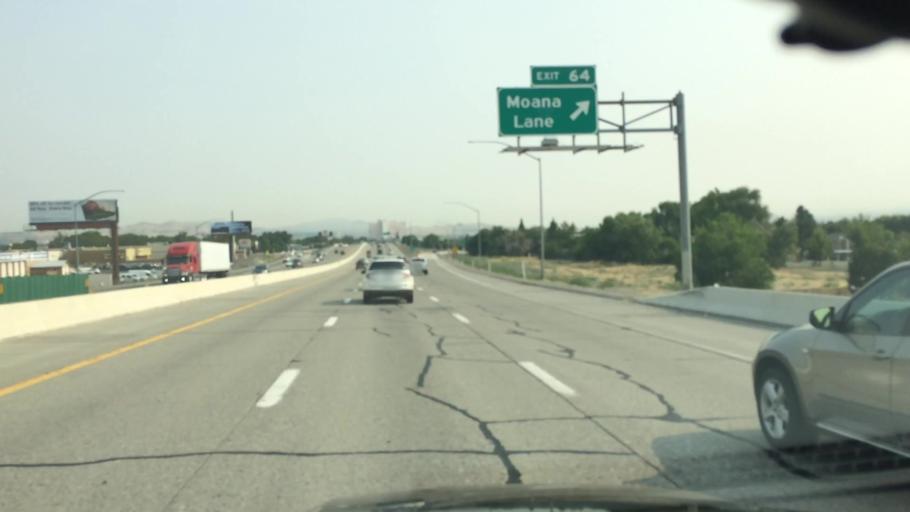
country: US
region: Nevada
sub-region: Washoe County
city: Reno
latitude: 39.4874
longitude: -119.7854
